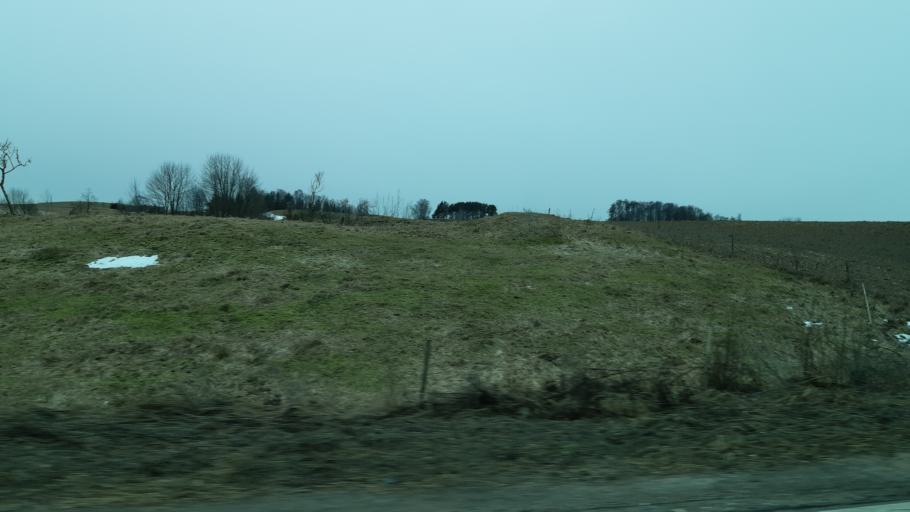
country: PL
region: Podlasie
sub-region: Suwalki
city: Suwalki
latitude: 54.3309
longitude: 22.9504
